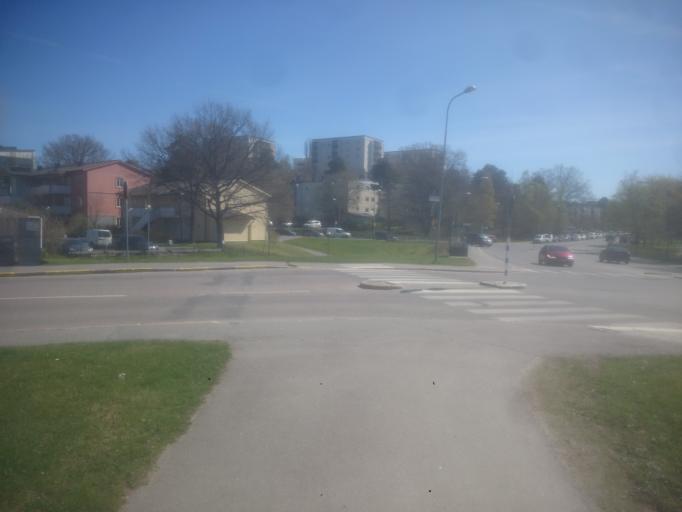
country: SE
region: Stockholm
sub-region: Stockholms Kommun
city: Arsta
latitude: 59.2435
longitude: 18.0813
